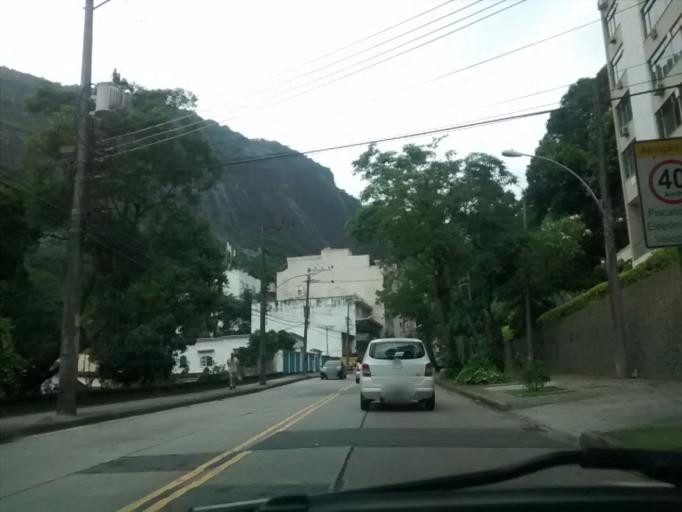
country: BR
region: Rio de Janeiro
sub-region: Rio De Janeiro
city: Rio de Janeiro
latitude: -22.9477
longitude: -43.2594
